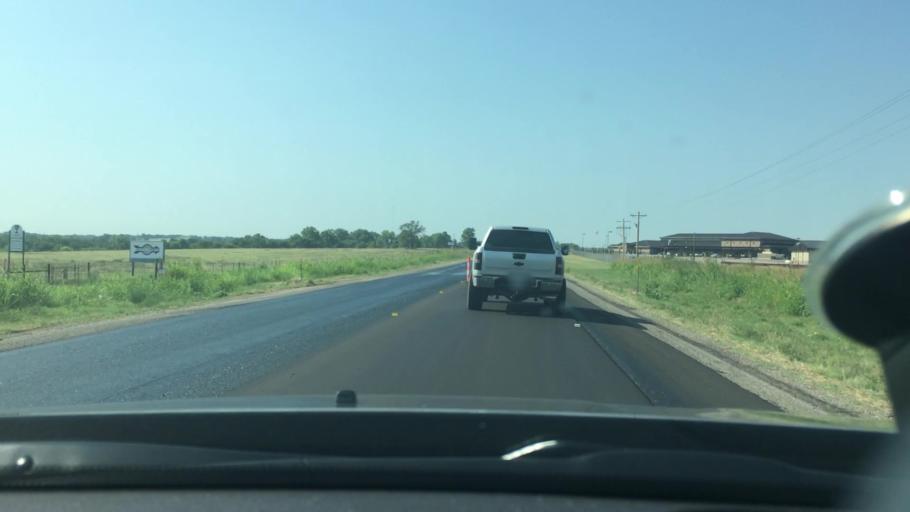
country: US
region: Oklahoma
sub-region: Garvin County
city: Lindsay
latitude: 34.8022
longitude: -97.5983
